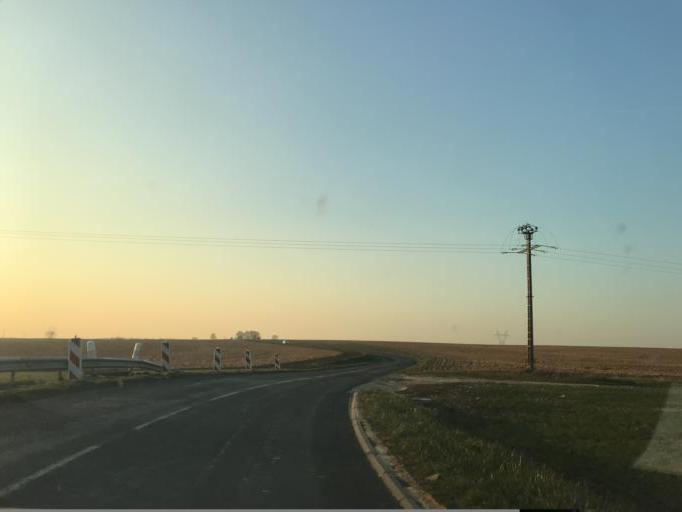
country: FR
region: Ile-de-France
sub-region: Departement de Seine-et-Marne
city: Juilly
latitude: 49.0128
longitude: 2.7456
